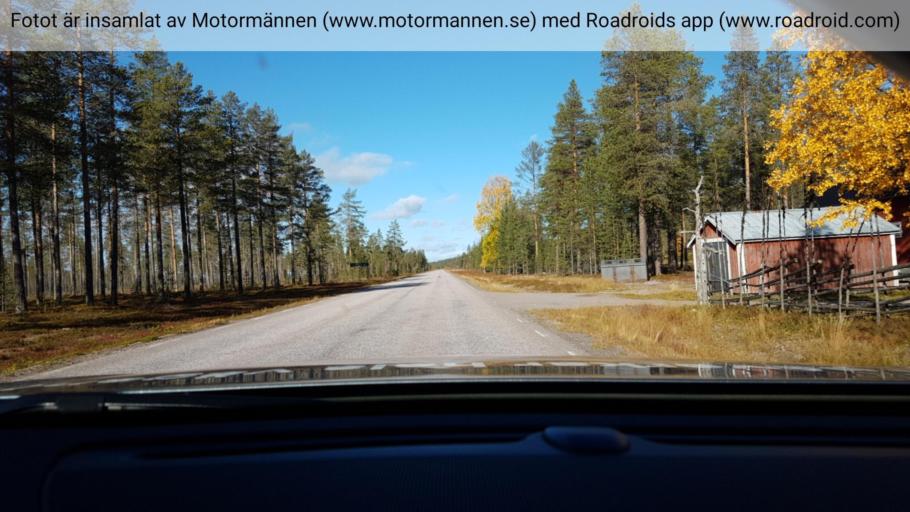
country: SE
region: Norrbotten
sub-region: Arvidsjaurs Kommun
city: Arvidsjaur
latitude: 65.6878
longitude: 18.7891
